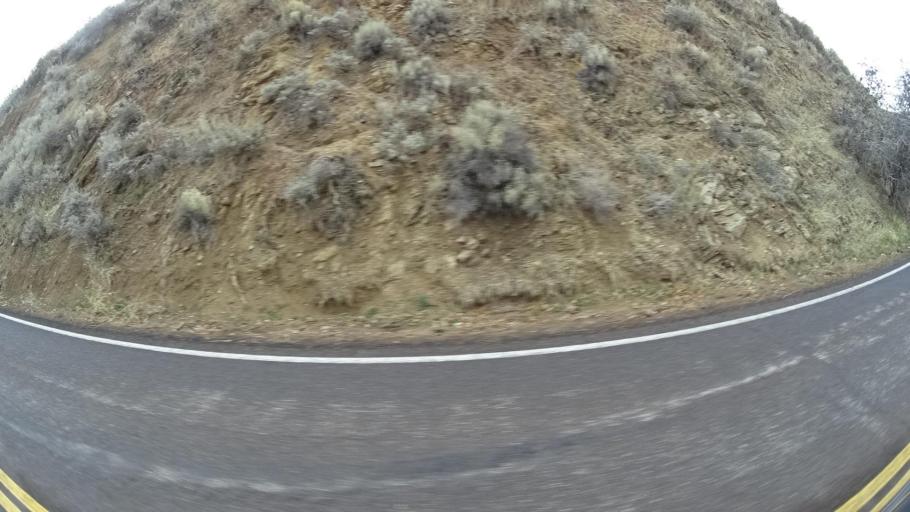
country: US
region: California
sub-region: Kern County
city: Golden Hills
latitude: 35.0937
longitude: -118.5542
